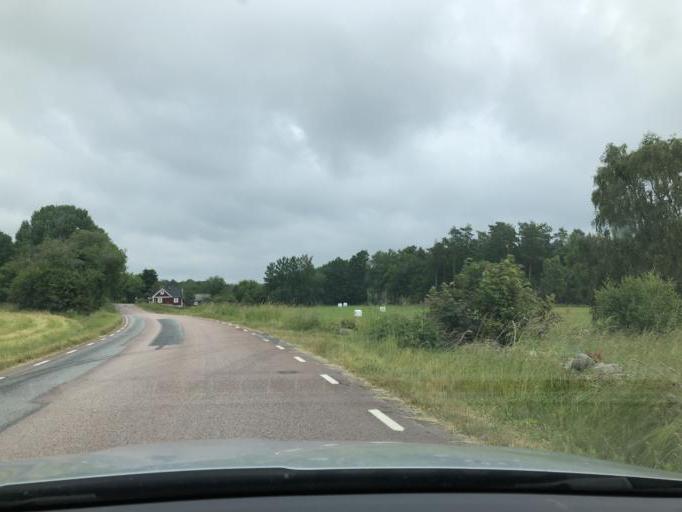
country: SE
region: Blekinge
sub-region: Solvesborgs Kommun
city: Soelvesborg
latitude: 56.1359
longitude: 14.6076
